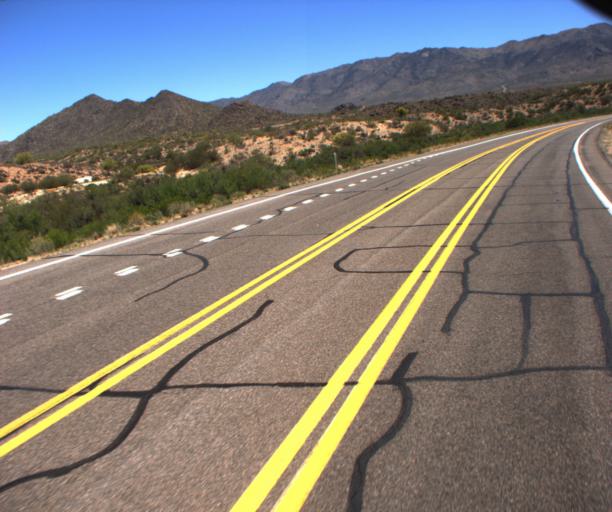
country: US
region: Arizona
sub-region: Yavapai County
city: Congress
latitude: 34.1640
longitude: -112.8433
